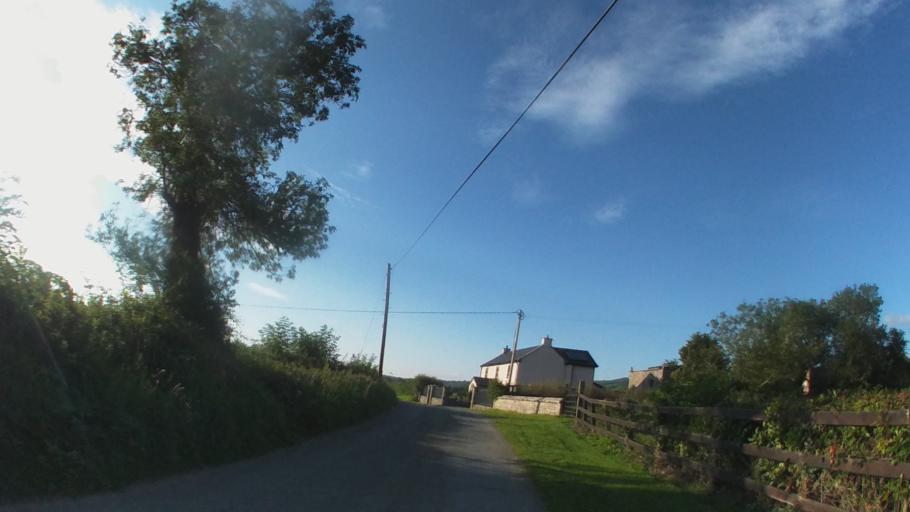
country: IE
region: Leinster
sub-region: Kilkenny
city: Kilkenny
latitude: 52.6924
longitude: -7.1893
